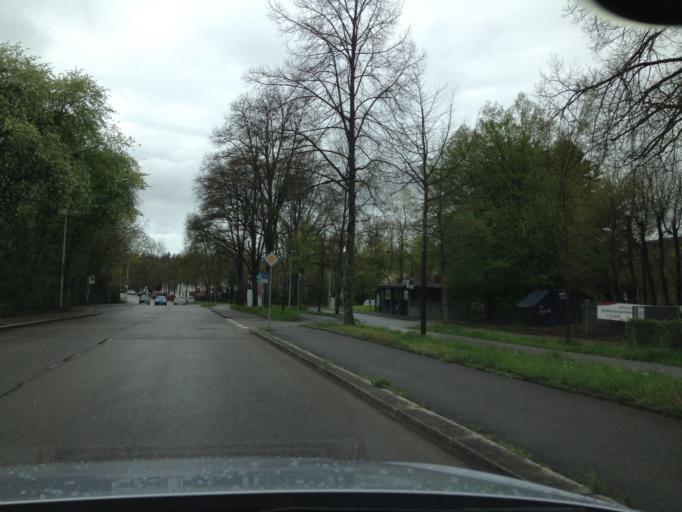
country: DE
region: Baden-Wuerttemberg
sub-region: Regierungsbezirk Stuttgart
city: Weinsberg
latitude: 49.1369
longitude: 9.2556
